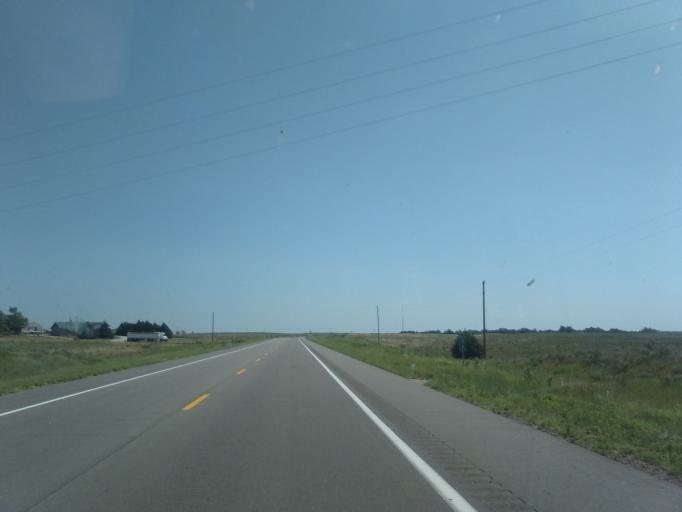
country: US
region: Nebraska
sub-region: Dundy County
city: Benkelman
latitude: 40.0677
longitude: -101.5223
